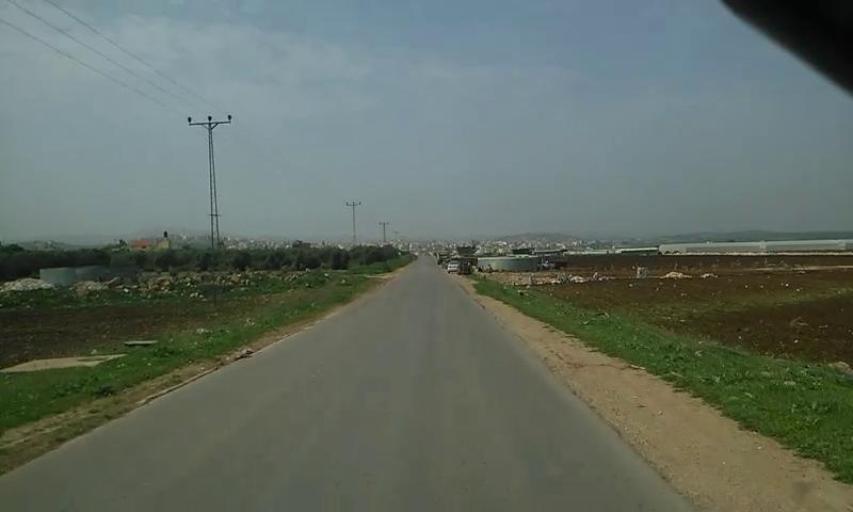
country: PS
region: West Bank
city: Kafr Dan
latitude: 32.4995
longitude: 35.2488
